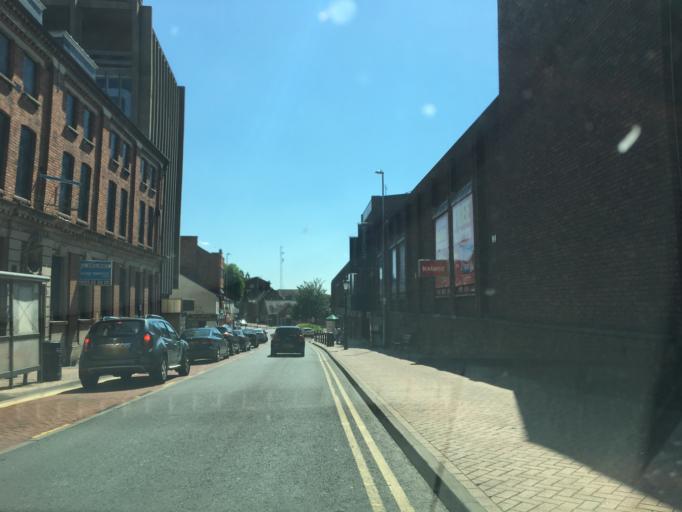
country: GB
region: England
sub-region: Northamptonshire
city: Wellingborough
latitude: 52.3019
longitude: -0.6917
